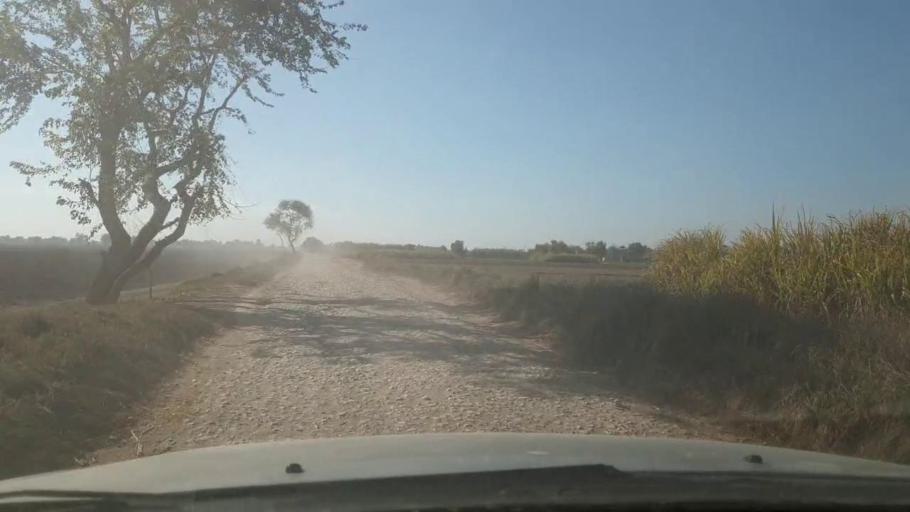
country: PK
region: Sindh
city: Ghotki
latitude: 27.9822
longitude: 69.2114
